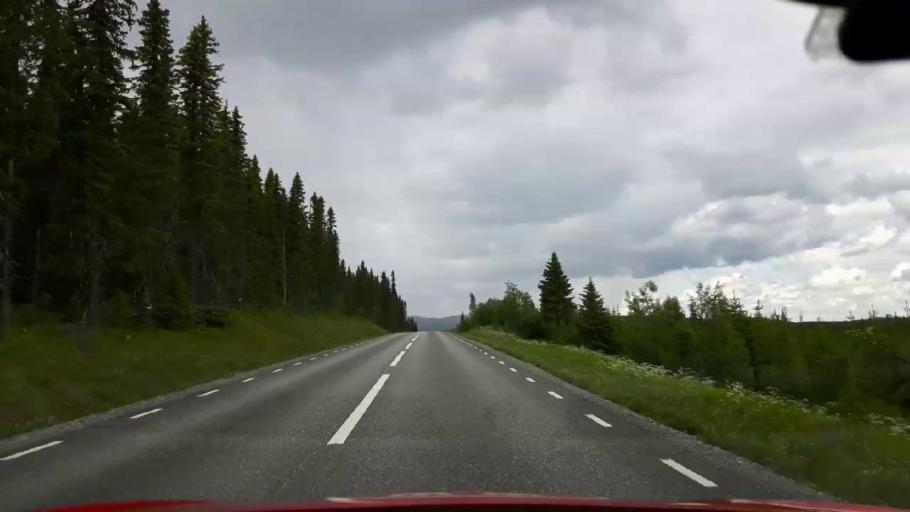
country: SE
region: Jaemtland
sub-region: Krokoms Kommun
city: Krokom
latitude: 63.7020
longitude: 14.3166
